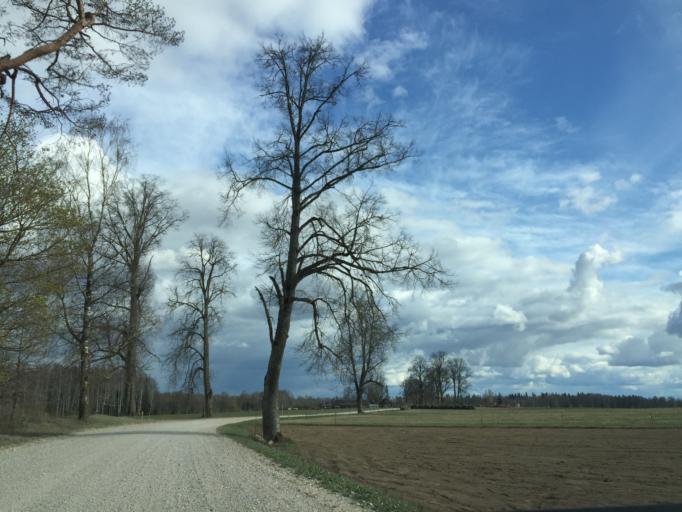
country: LV
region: Burtnieki
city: Matisi
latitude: 57.6087
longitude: 25.0769
